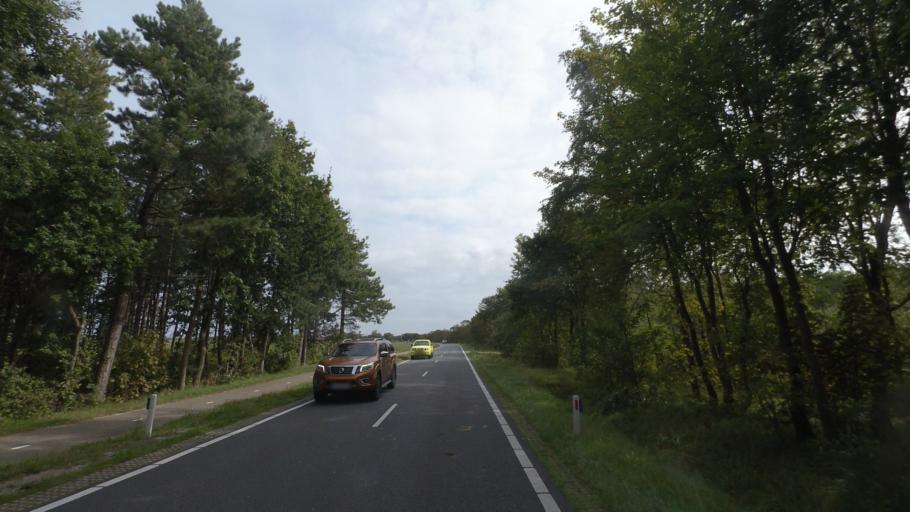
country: NL
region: Friesland
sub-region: Gemeente Ameland
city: Nes
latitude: 53.4457
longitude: 5.7143
